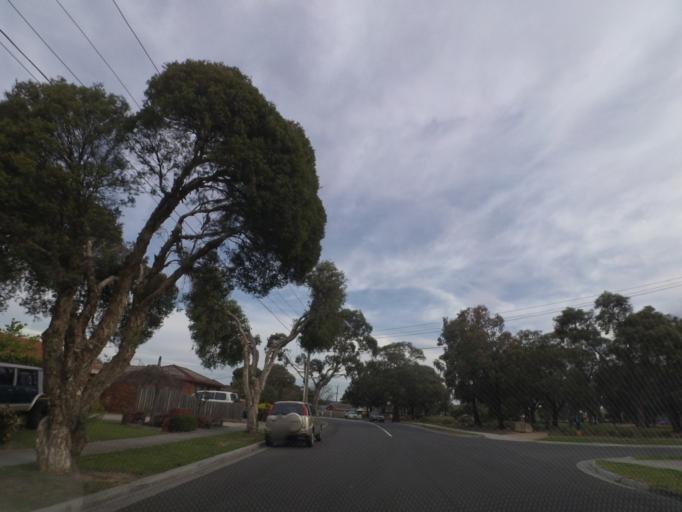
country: AU
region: Victoria
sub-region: Knox
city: Knoxfield
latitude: -37.8847
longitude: 145.2613
